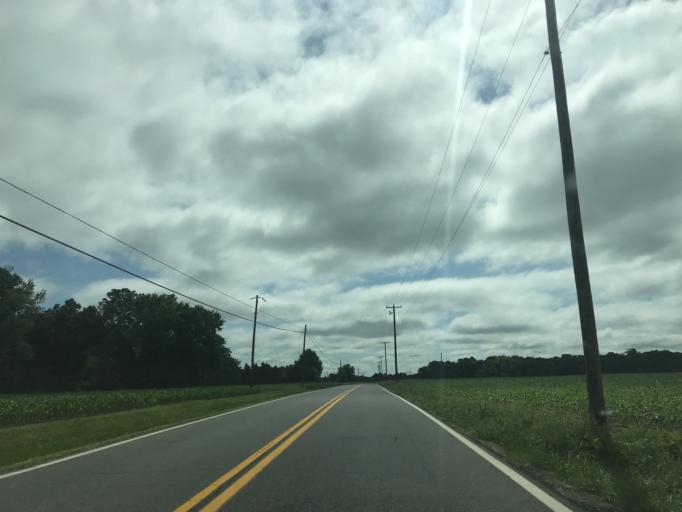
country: US
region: Maryland
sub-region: Caroline County
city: Ridgely
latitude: 38.8856
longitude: -75.9655
